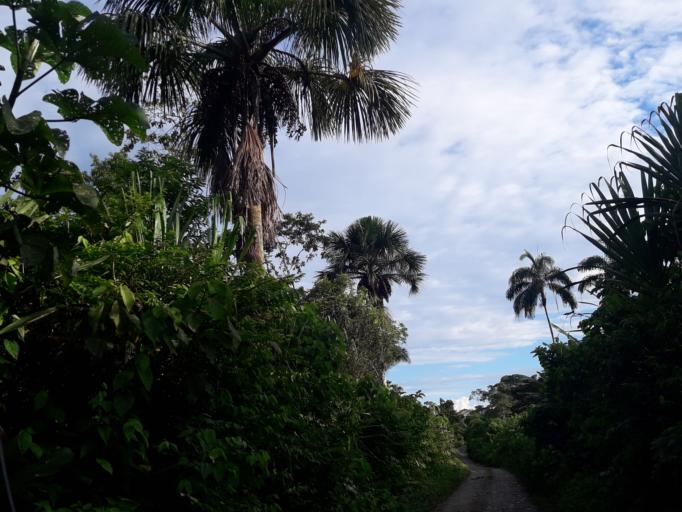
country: EC
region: Orellana
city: Boca Suno
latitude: -0.8910
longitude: -77.3065
